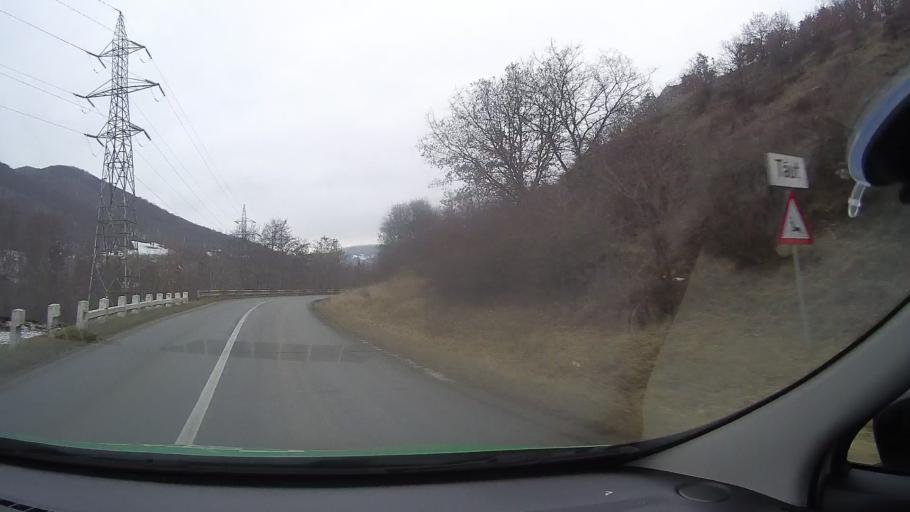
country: RO
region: Alba
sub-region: Comuna Metes
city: Metes
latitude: 46.1017
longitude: 23.4550
